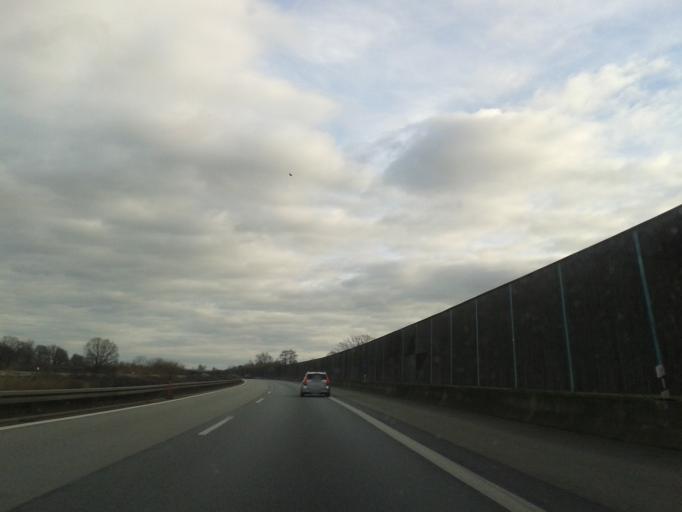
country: DE
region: Saxony
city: Malschwitz
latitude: 51.2062
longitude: 14.5226
